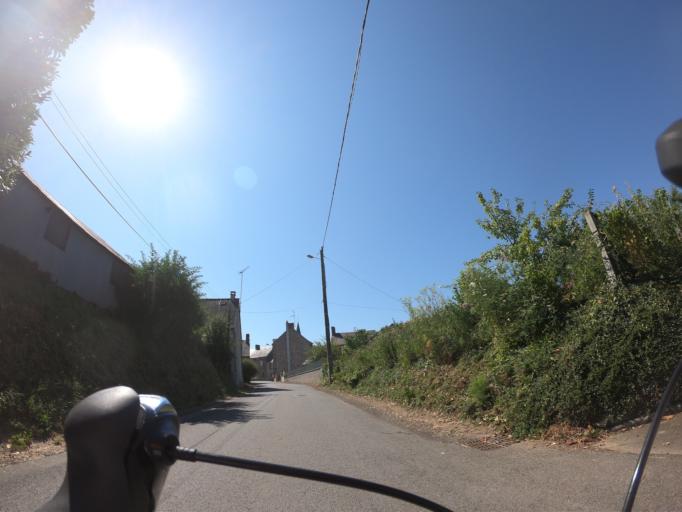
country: FR
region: Lower Normandy
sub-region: Departement de la Manche
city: Barenton
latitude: 48.5666
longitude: -0.7999
